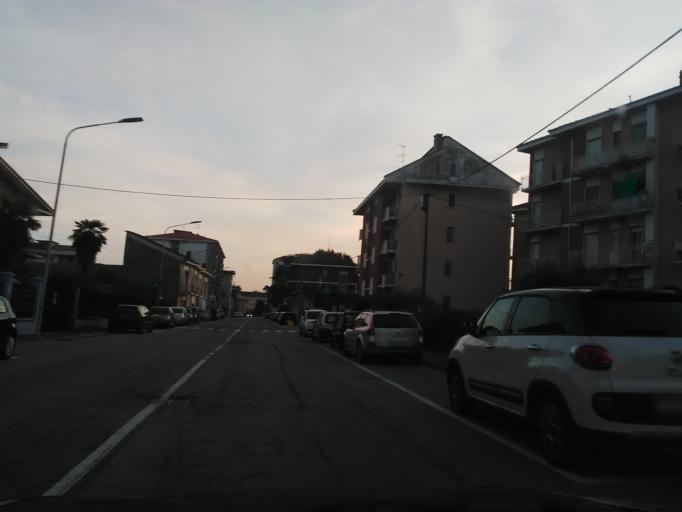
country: IT
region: Piedmont
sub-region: Provincia di Vercelli
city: Santhia
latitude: 45.3675
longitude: 8.1798
